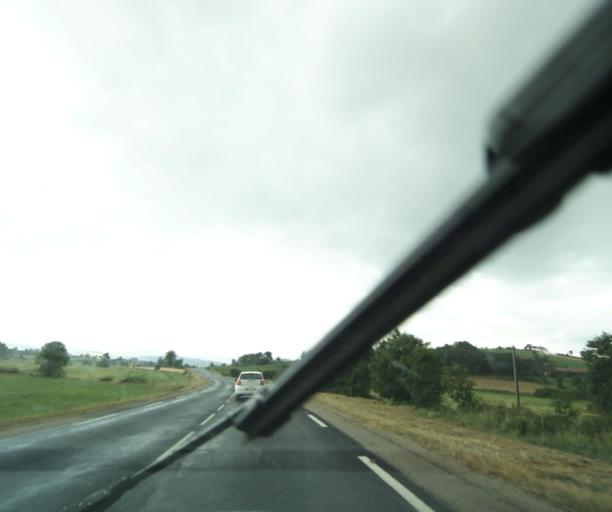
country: FR
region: Auvergne
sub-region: Departement de la Haute-Loire
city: Espaly-Saint-Marcel
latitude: 45.0245
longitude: 3.8445
